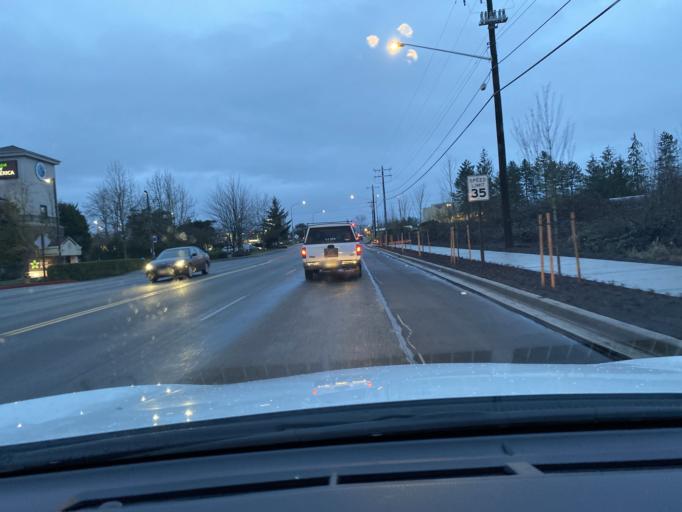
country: US
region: Washington
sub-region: Snohomish County
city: Mukilteo
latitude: 47.8890
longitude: -122.2877
